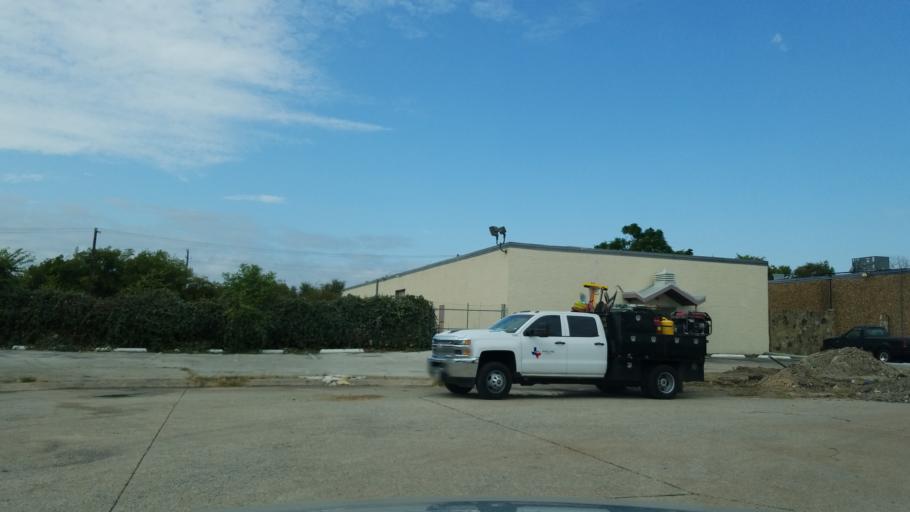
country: US
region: Texas
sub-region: Dallas County
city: Garland
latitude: 32.8988
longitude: -96.6908
